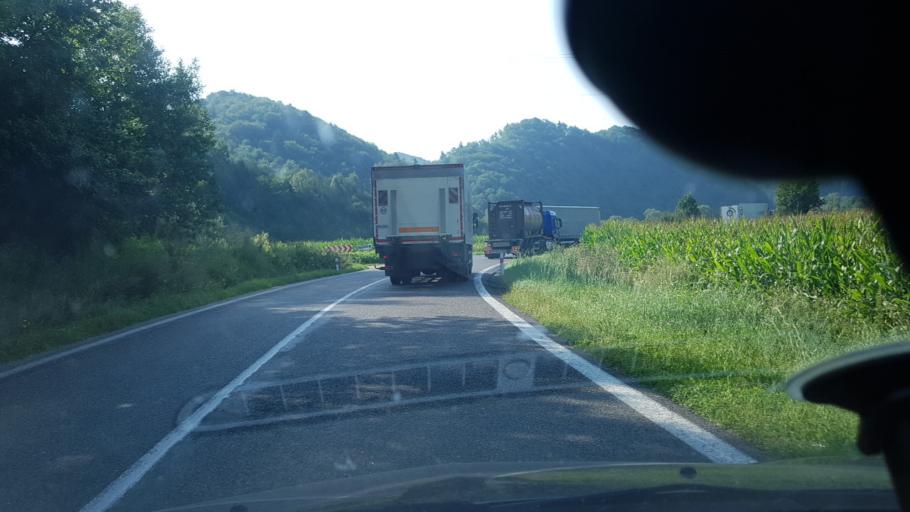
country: SK
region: Zilinsky
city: Tvrdosin
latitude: 49.2758
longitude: 19.4628
